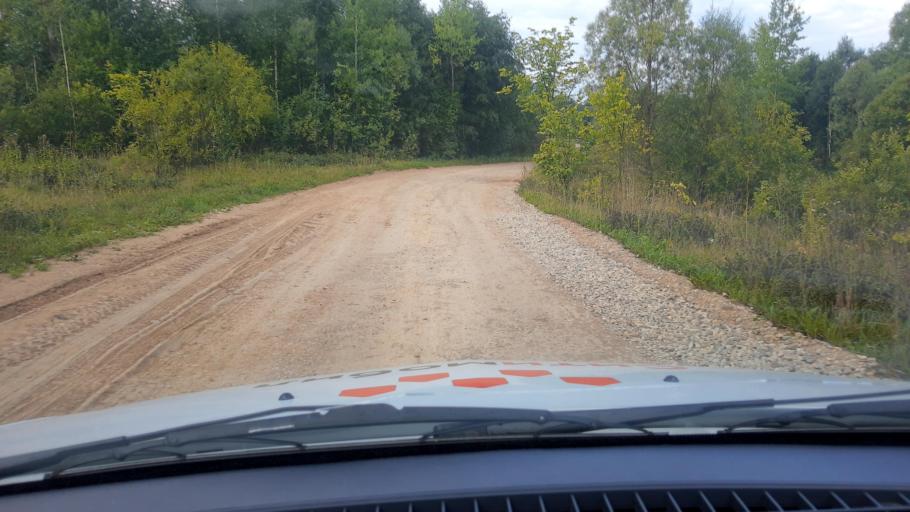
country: RU
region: Bashkortostan
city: Kabakovo
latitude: 54.7031
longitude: 56.1376
